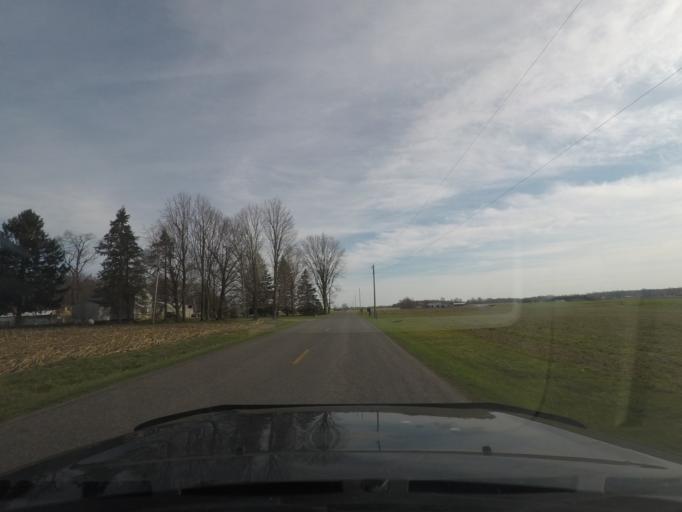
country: US
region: Indiana
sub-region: Elkhart County
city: Dunlap
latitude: 41.5717
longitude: -85.9250
